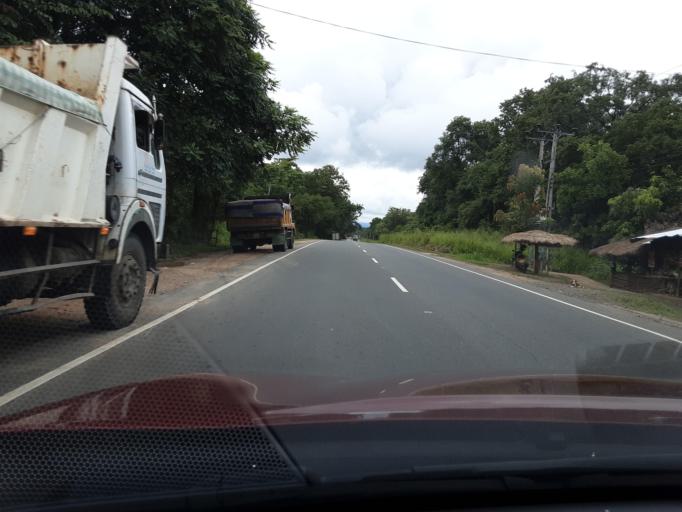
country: LK
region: Uva
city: Badulla
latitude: 7.3979
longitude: 81.1118
